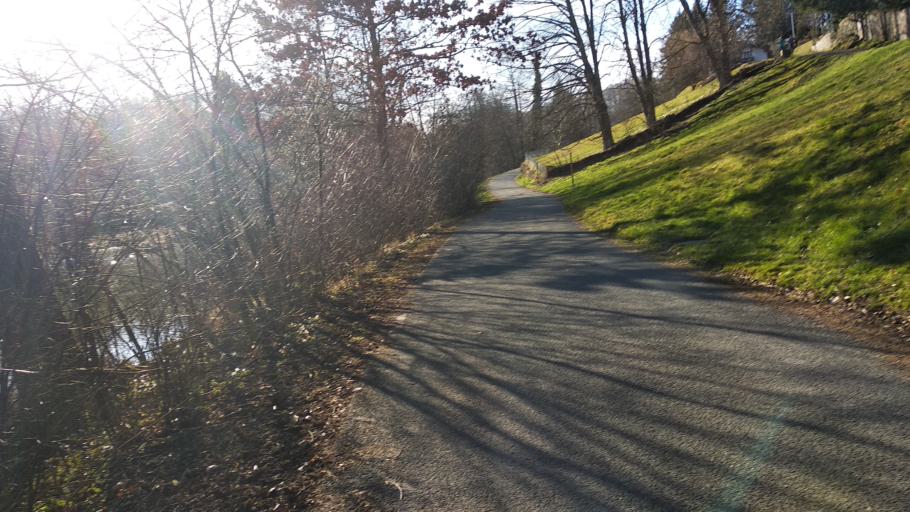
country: DE
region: Bavaria
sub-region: Upper Bavaria
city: Ebersberg
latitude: 48.0825
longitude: 11.9626
